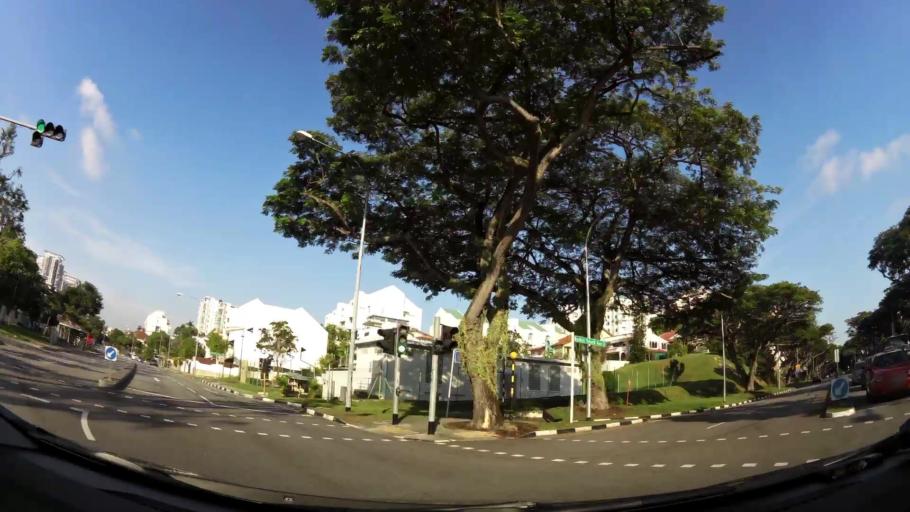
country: SG
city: Singapore
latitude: 1.3164
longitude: 103.9454
